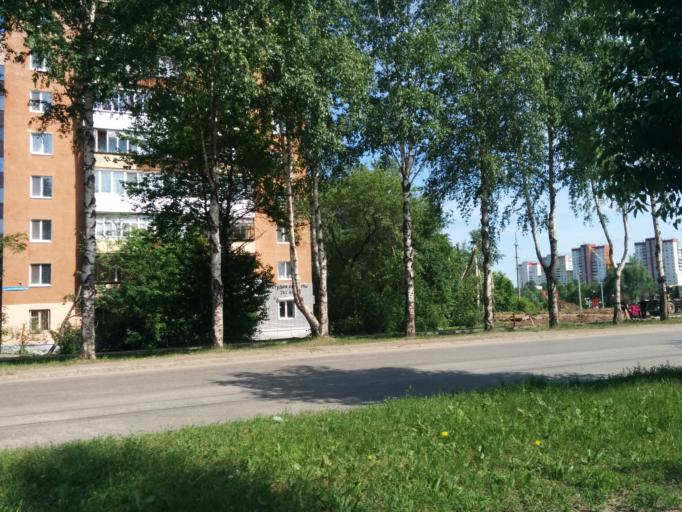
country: RU
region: Perm
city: Perm
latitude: 58.0103
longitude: 56.2940
